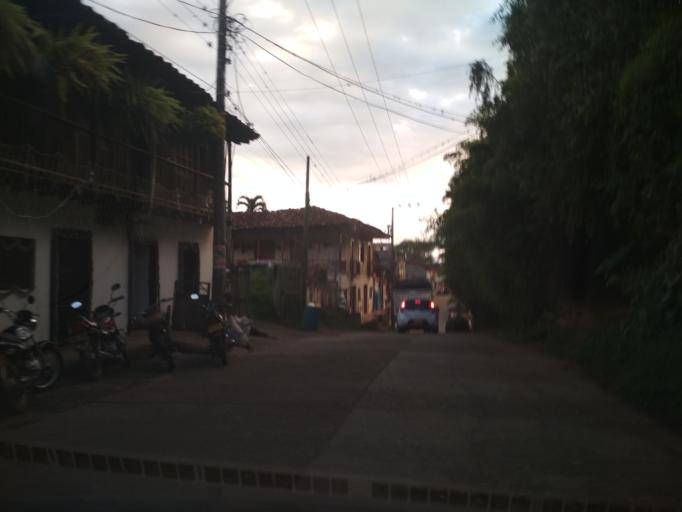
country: CO
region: Valle del Cauca
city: Calimita
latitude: 3.9343
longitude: -76.4834
